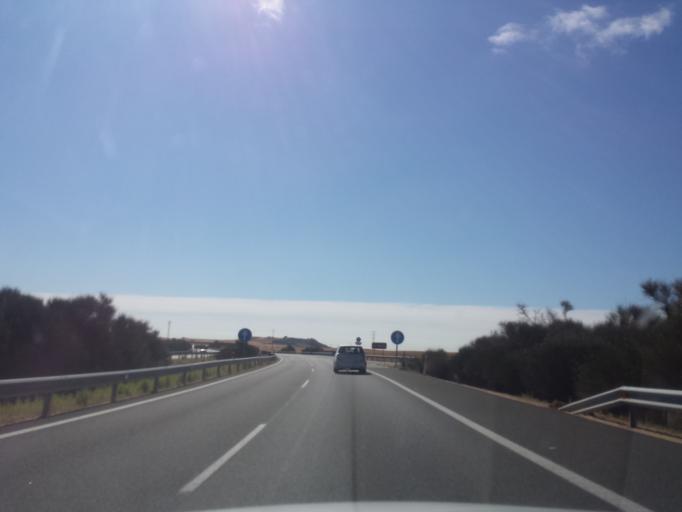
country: ES
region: Castille and Leon
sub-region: Provincia de Valladolid
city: Mota del Marques
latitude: 41.6294
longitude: -5.1833
